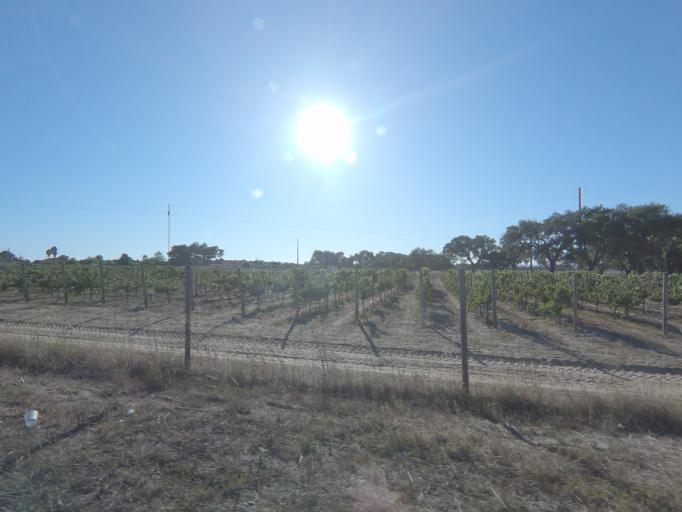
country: PT
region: Setubal
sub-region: Palmela
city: Quinta do Anjo
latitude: 38.5407
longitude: -8.9858
